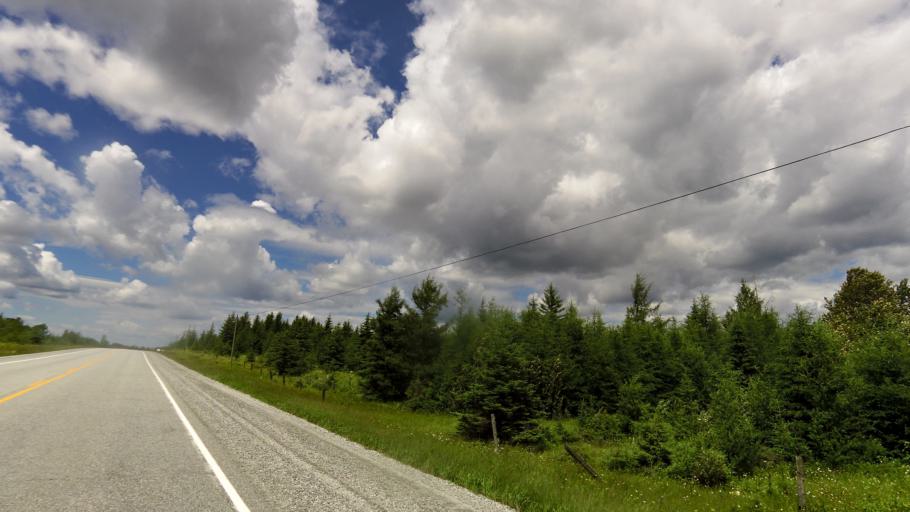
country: CA
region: Ontario
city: Kapuskasing
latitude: 49.2858
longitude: -81.7684
